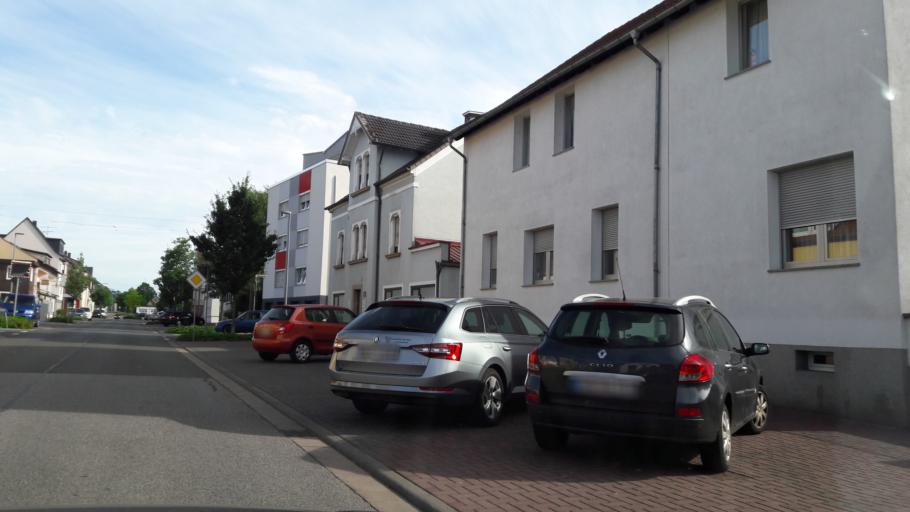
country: DE
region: Saarland
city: Homburg
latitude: 49.3328
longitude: 7.3365
